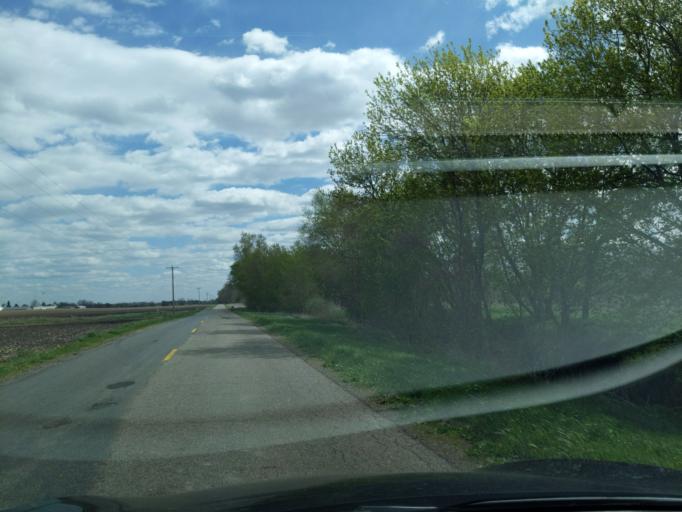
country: US
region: Michigan
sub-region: Ingham County
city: Mason
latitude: 42.5335
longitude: -84.5422
